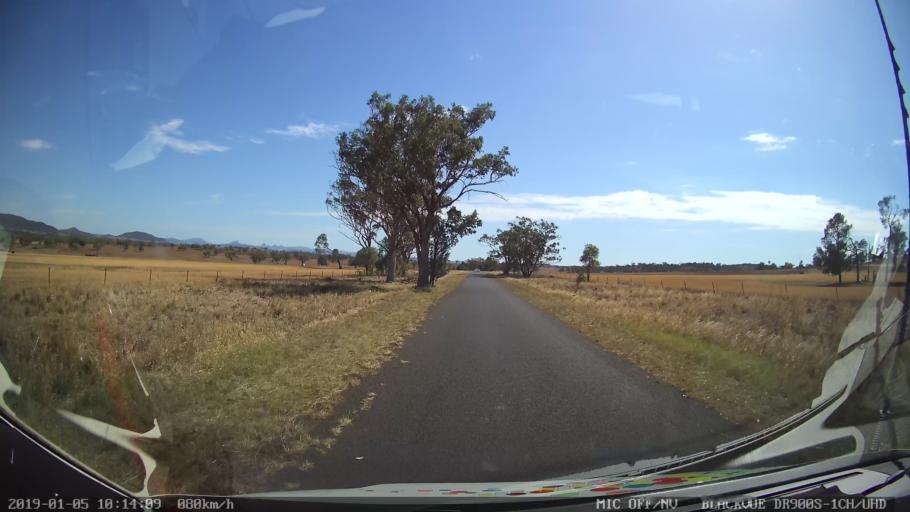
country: AU
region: New South Wales
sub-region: Gilgandra
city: Gilgandra
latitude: -31.5955
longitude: 148.9317
